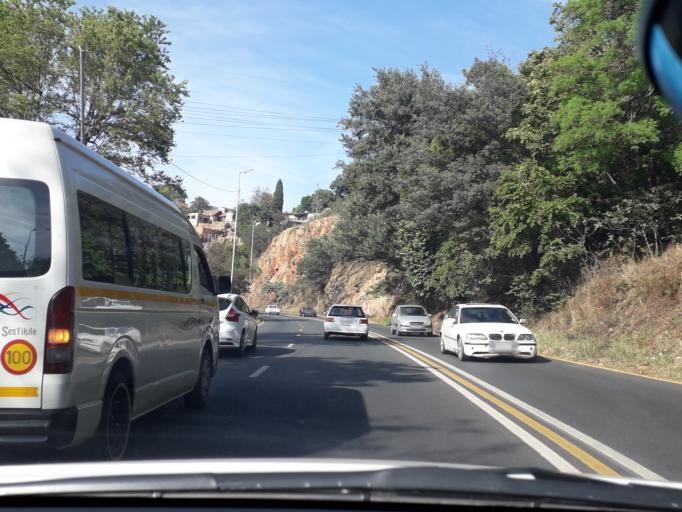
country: ZA
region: Gauteng
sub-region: City of Johannesburg Metropolitan Municipality
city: Roodepoort
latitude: -26.1312
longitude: 27.8939
